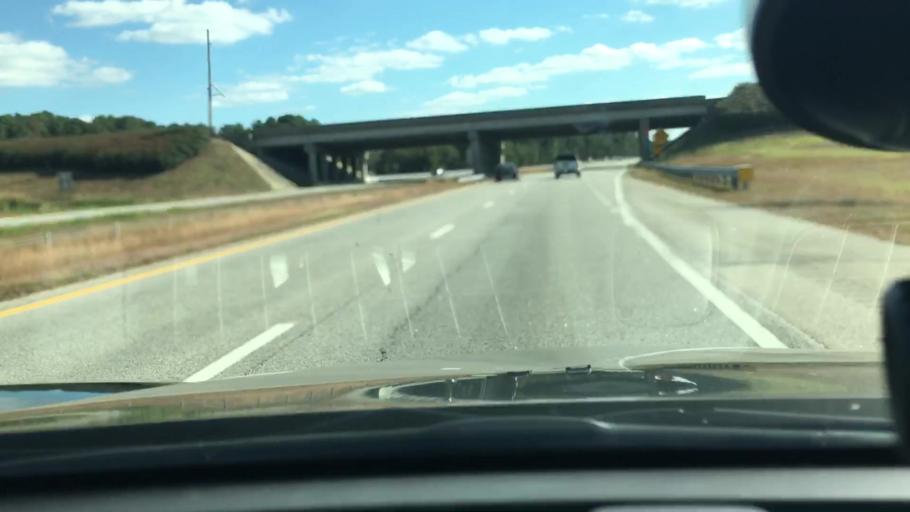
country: US
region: North Carolina
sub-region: Wilson County
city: Lucama
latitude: 35.7626
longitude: -78.0294
